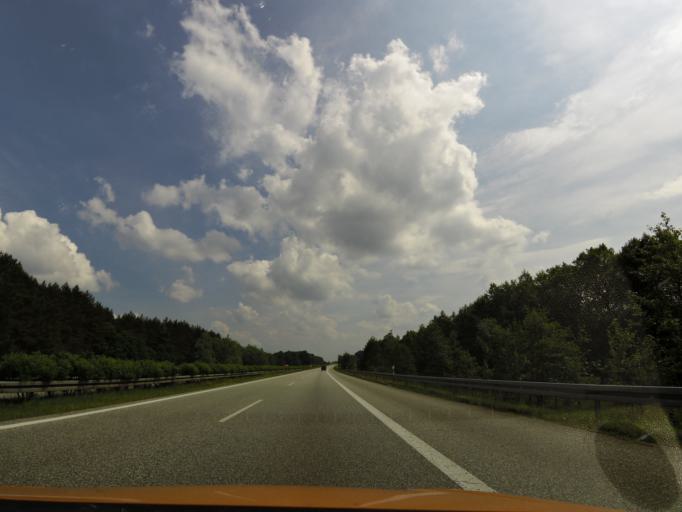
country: DE
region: Mecklenburg-Vorpommern
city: Siggelkow
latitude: 53.3265
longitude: 11.8831
